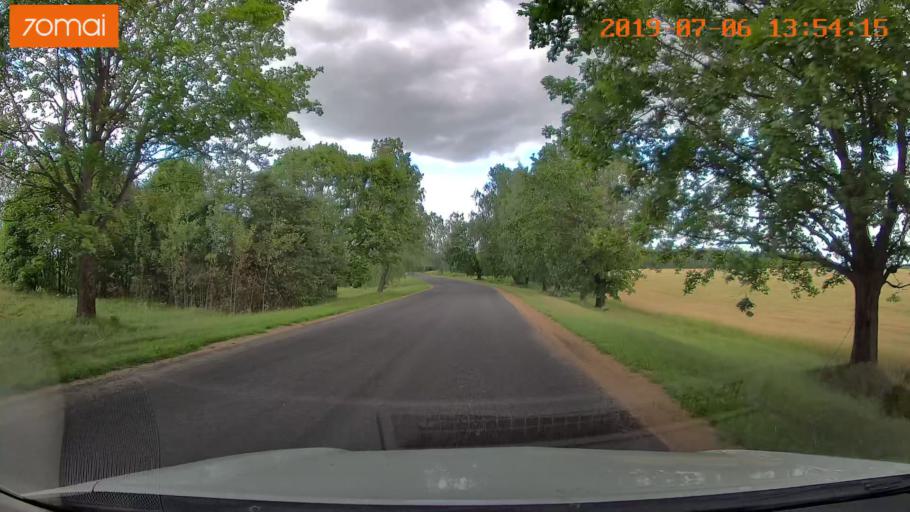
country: BY
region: Minsk
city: Ivyanyets
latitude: 53.7439
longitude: 26.8218
